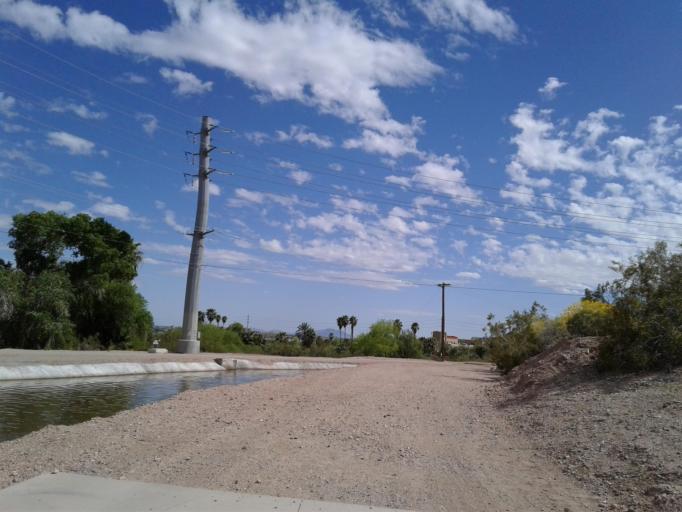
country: US
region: Arizona
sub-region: Maricopa County
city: Tempe Junction
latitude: 33.4505
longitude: -111.9400
